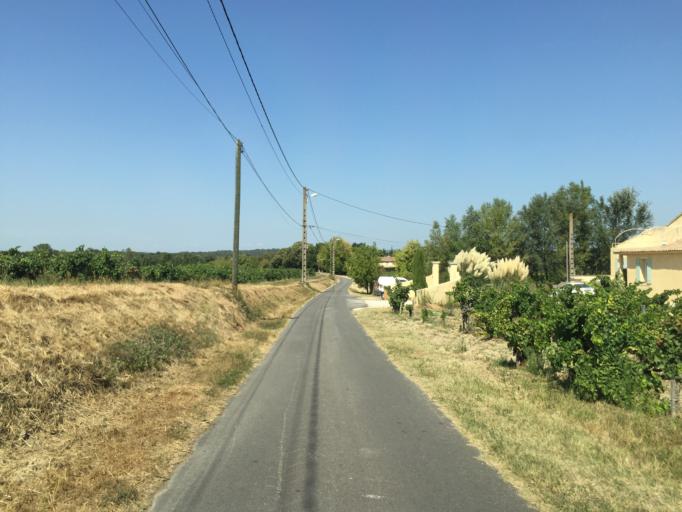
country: FR
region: Provence-Alpes-Cote d'Azur
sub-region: Departement du Vaucluse
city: Chateauneuf-du-Pape
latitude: 44.0967
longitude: 4.8167
